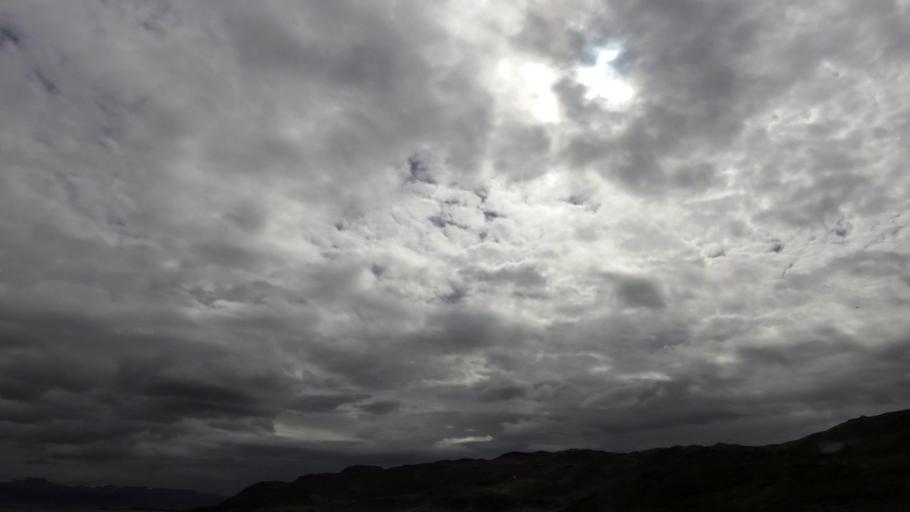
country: IS
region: West
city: Stykkisholmur
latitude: 65.5416
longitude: -22.1112
